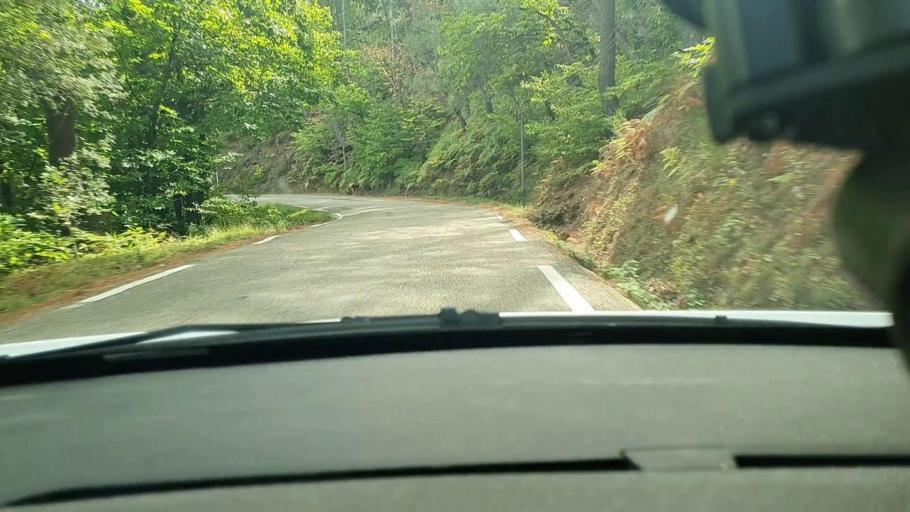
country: FR
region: Languedoc-Roussillon
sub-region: Departement du Gard
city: Besseges
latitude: 44.3068
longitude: 4.0518
